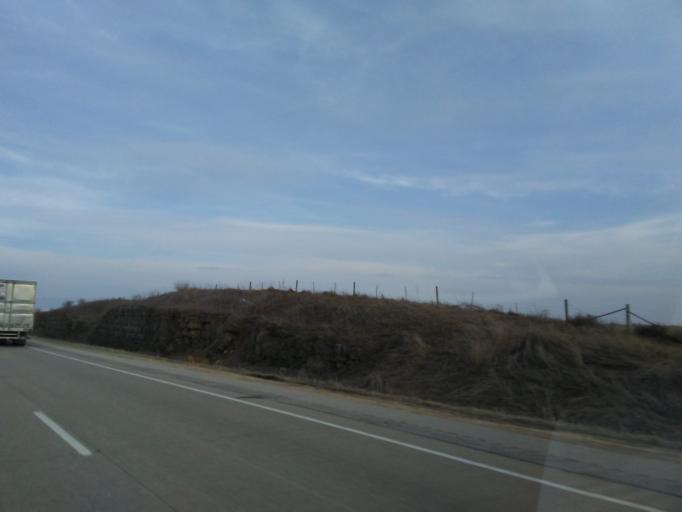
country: US
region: Wisconsin
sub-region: Iowa County
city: Barneveld
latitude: 43.0101
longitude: -89.8408
